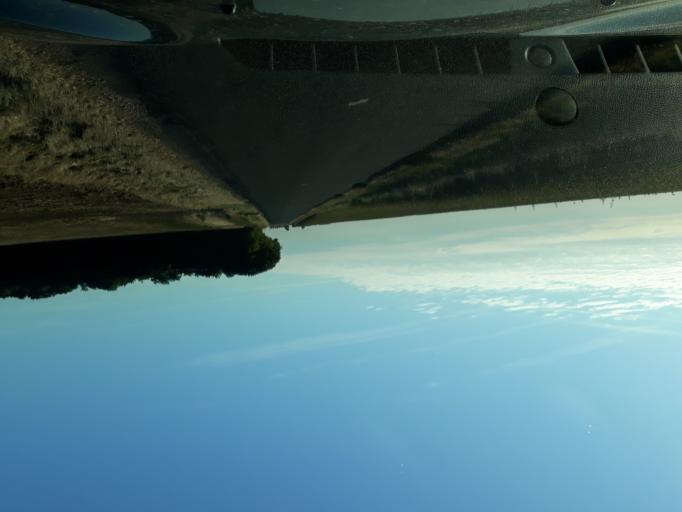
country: FR
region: Centre
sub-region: Departement du Loir-et-Cher
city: Ouzouer-le-Marche
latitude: 47.9608
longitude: 1.5484
